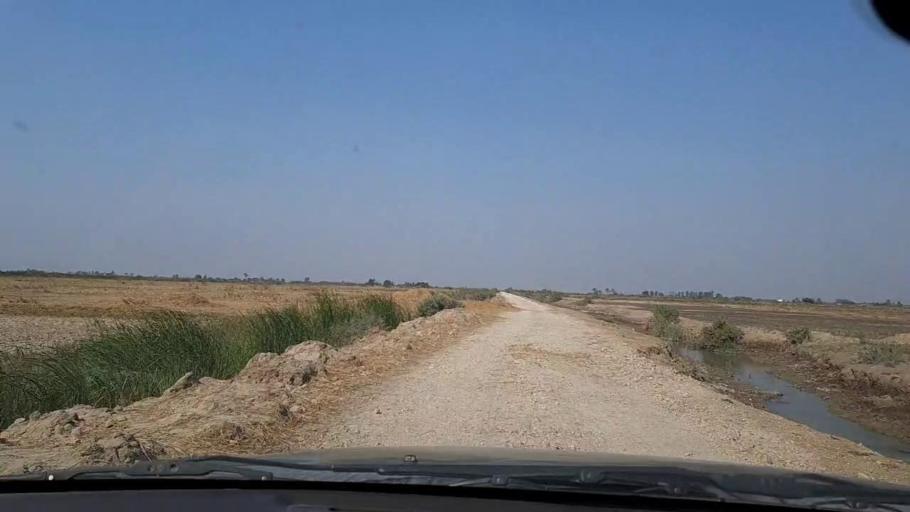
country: PK
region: Sindh
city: Mirpur Sakro
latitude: 24.3678
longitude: 67.6830
